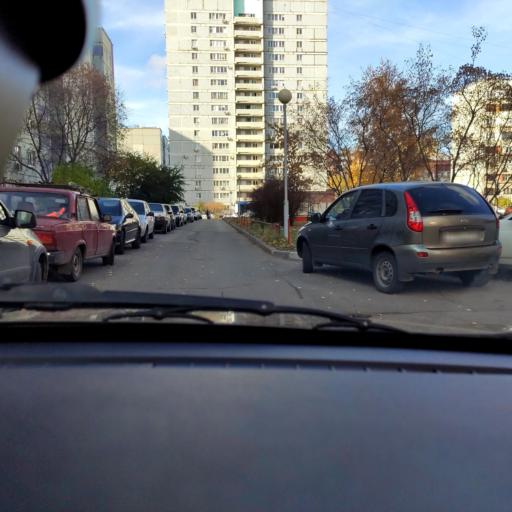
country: RU
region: Samara
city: Tol'yatti
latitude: 53.5392
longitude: 49.3378
